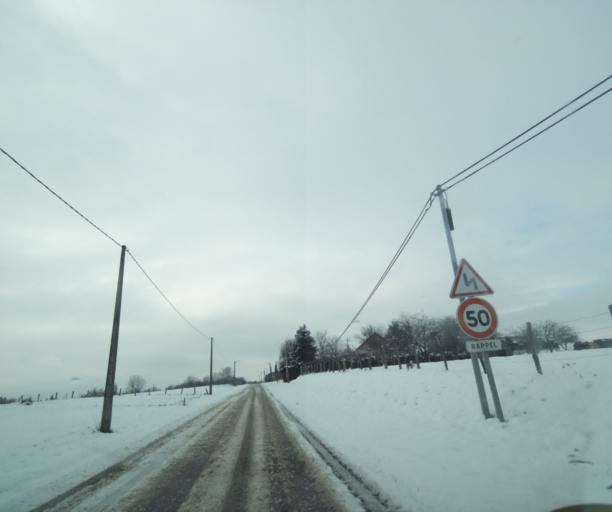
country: FR
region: Champagne-Ardenne
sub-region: Departement de la Haute-Marne
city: Montier-en-Der
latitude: 48.5209
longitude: 4.7024
